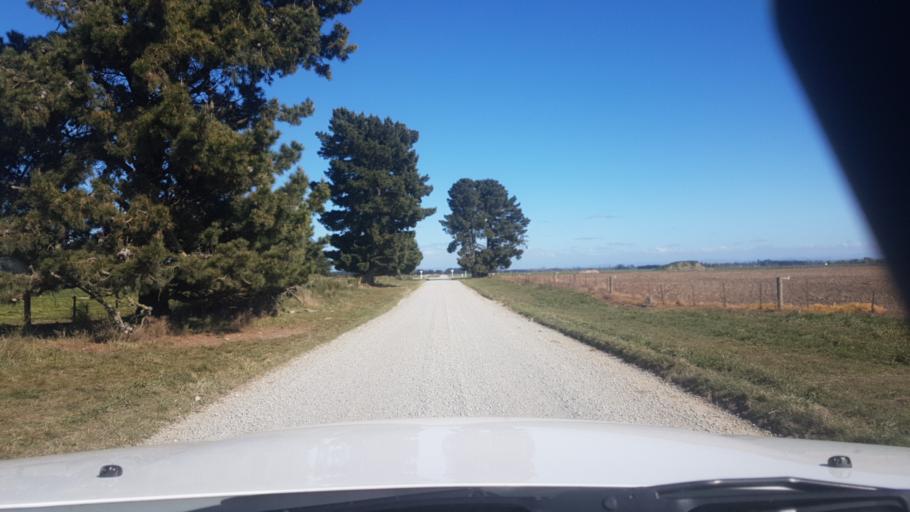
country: NZ
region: Canterbury
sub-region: Timaru District
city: Pleasant Point
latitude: -44.1359
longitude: 171.3829
